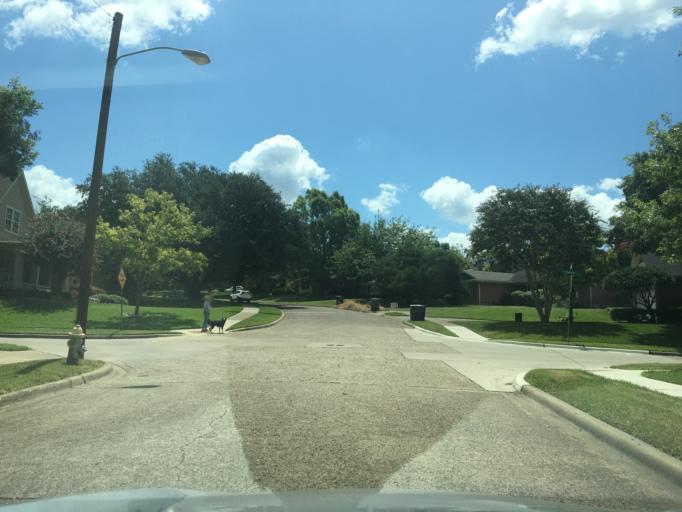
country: US
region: Texas
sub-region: Dallas County
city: Richardson
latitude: 32.8689
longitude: -96.7136
